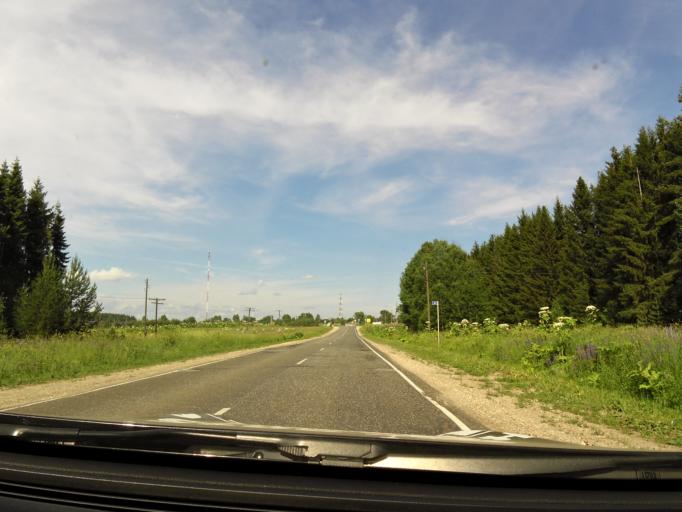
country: RU
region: Kirov
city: Belaya Kholunitsa
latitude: 58.8006
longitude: 50.5353
